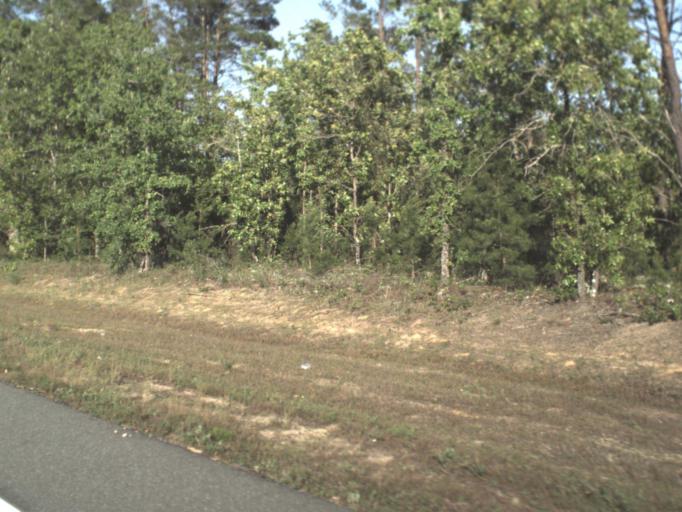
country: US
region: Florida
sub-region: Gadsden County
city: Gretna
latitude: 30.4538
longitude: -84.7506
